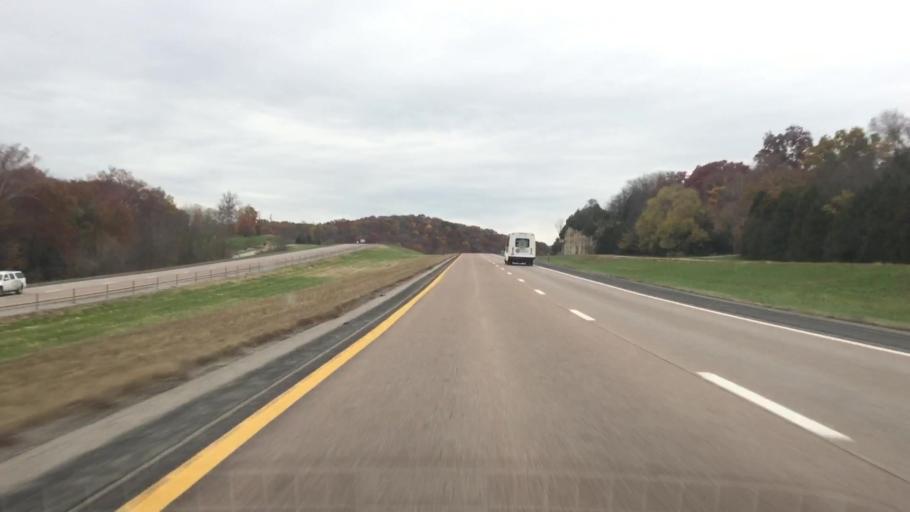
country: US
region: Missouri
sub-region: Cole County
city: Jefferson City
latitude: 38.6559
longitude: -92.2165
